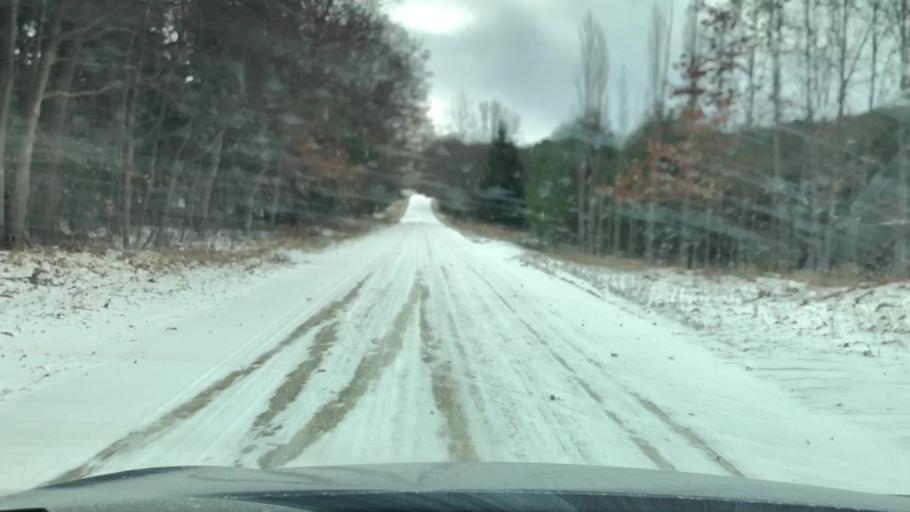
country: US
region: Michigan
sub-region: Antrim County
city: Elk Rapids
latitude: 44.9577
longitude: -85.5155
